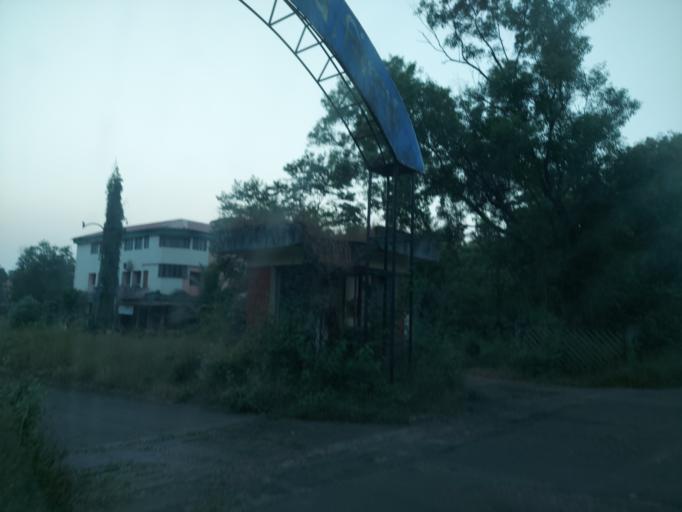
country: IN
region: Maharashtra
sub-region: Sindhudurg
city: Kudal
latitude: 16.1137
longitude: 73.6994
